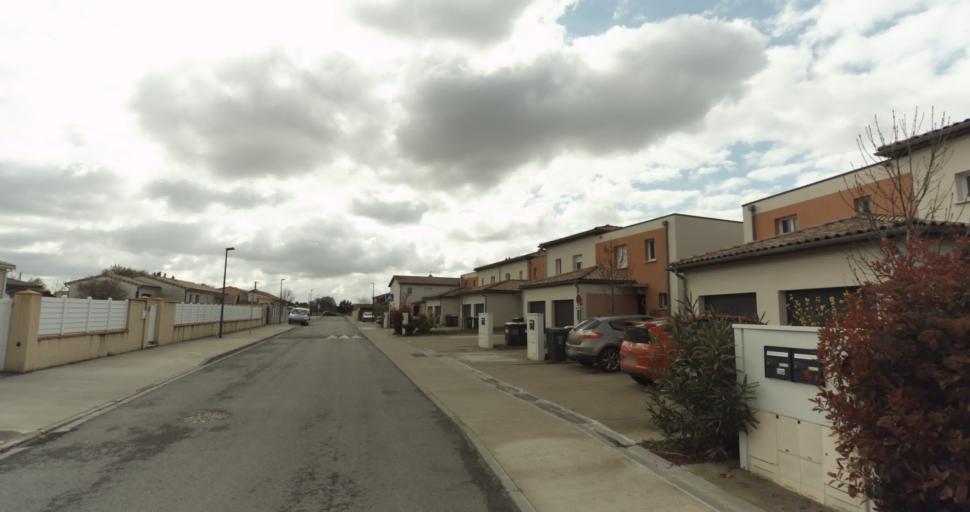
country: FR
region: Midi-Pyrenees
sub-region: Departement de la Haute-Garonne
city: Auterive
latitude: 43.3486
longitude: 1.4620
